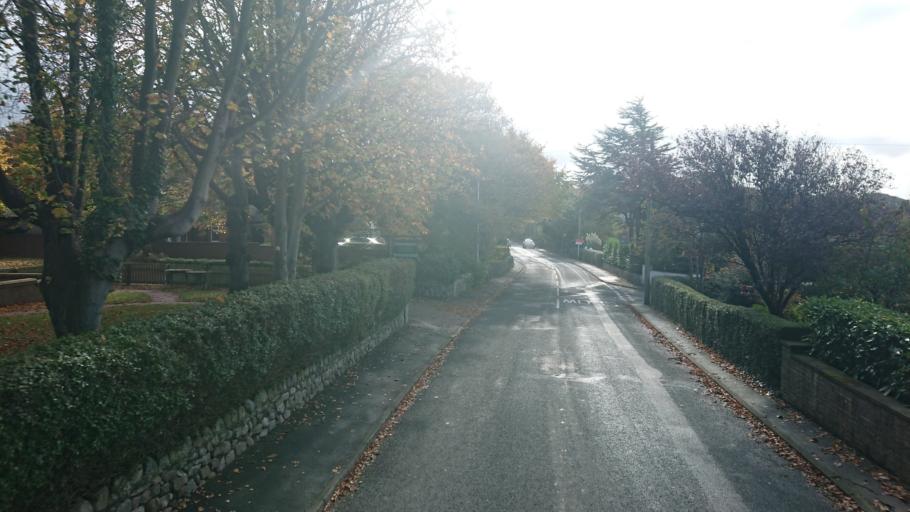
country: GB
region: England
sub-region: Lancashire
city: Bolton le Sands
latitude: 54.0880
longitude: -2.8103
